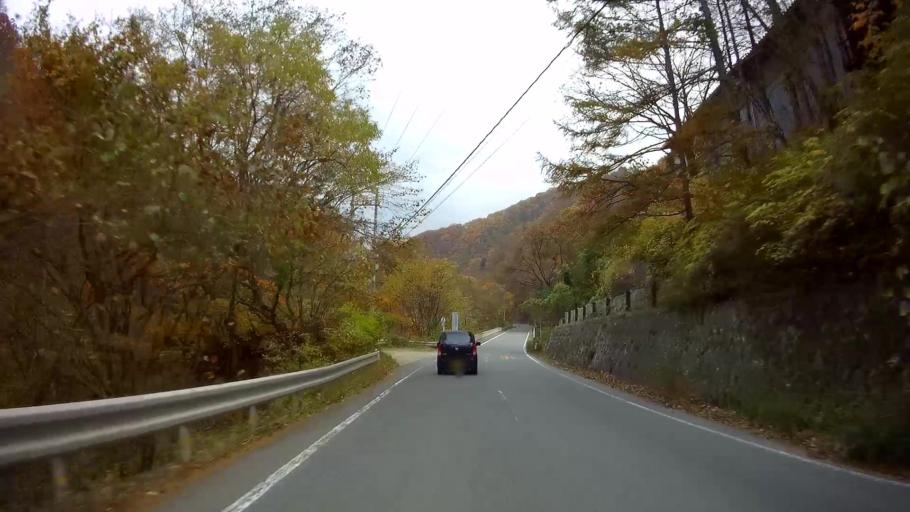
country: JP
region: Gunma
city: Nakanojomachi
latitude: 36.6339
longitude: 138.6544
